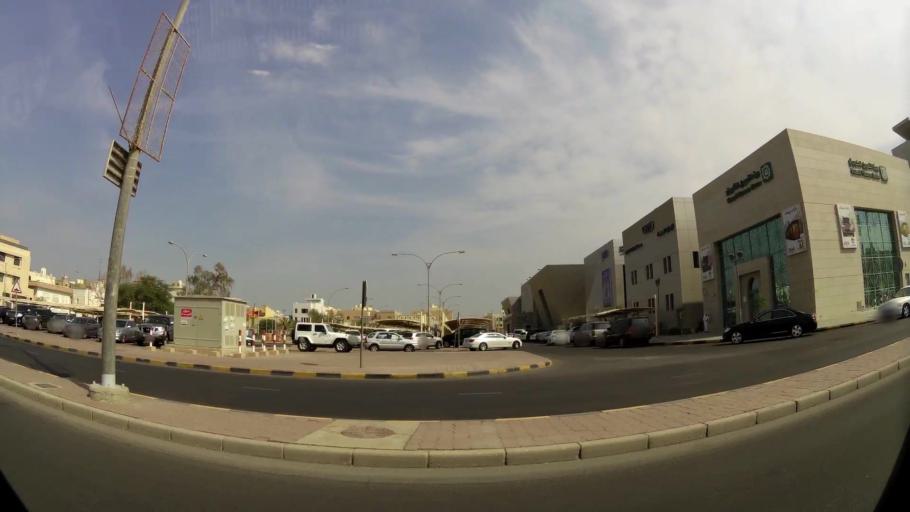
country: KW
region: Al Asimah
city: Ash Shamiyah
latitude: 29.3399
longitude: 47.9616
